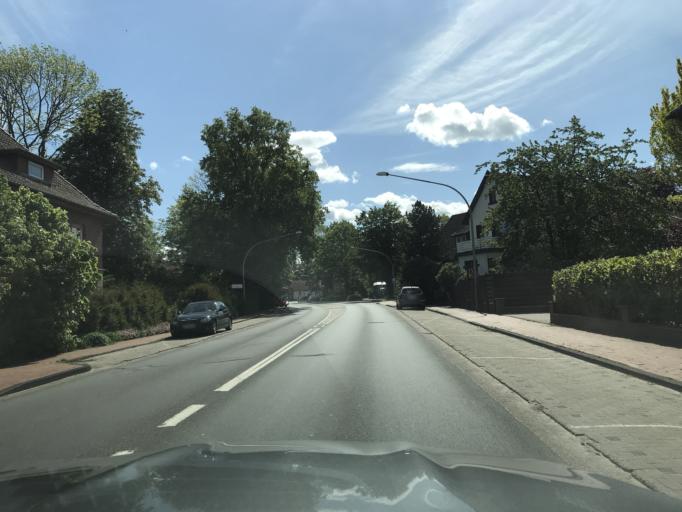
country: DE
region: North Rhine-Westphalia
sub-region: Regierungsbezirk Munster
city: Westerkappeln
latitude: 52.3132
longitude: 7.8755
